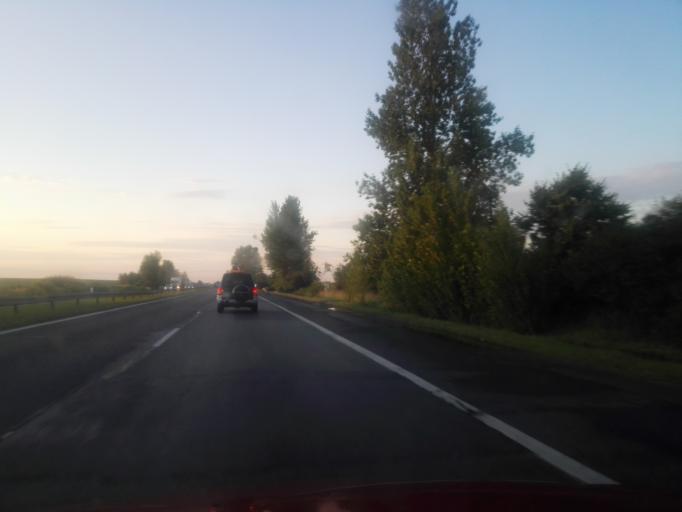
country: PL
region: Silesian Voivodeship
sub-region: Czestochowa
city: Czestochowa
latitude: 50.8509
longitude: 19.1519
